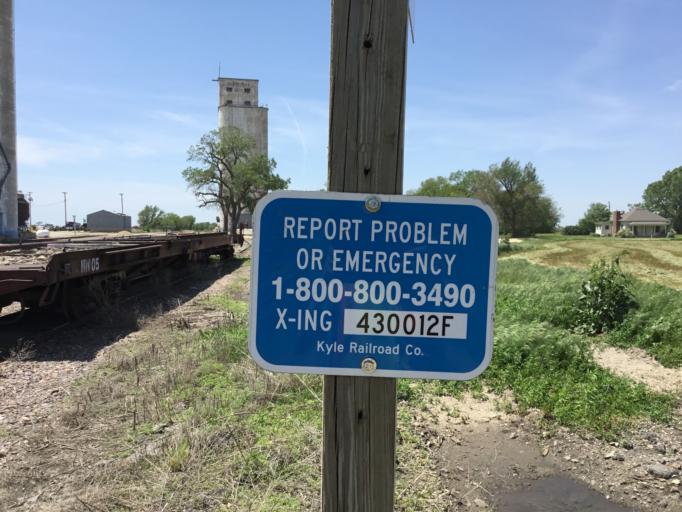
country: US
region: Kansas
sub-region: Mitchell County
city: Beloit
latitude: 39.5441
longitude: -97.9530
